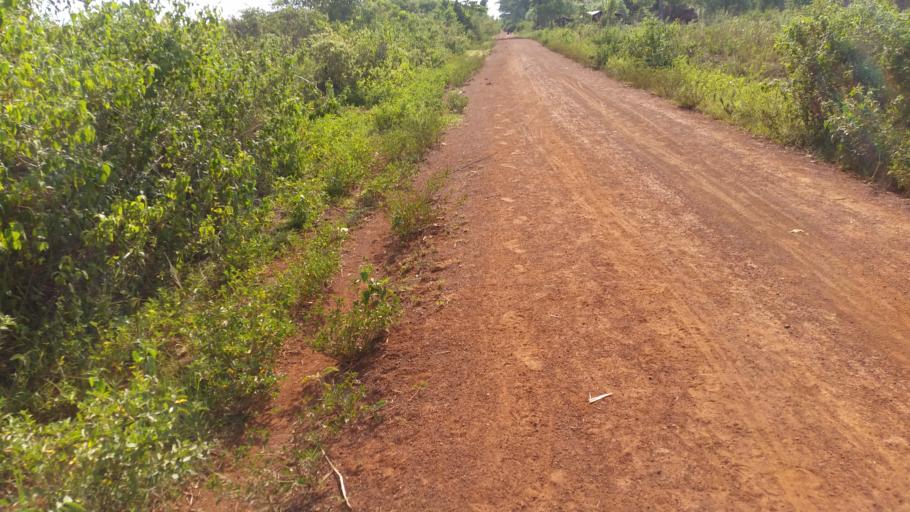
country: UG
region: Eastern Region
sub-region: Busia District
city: Busia
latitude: 0.5496
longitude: 34.0048
